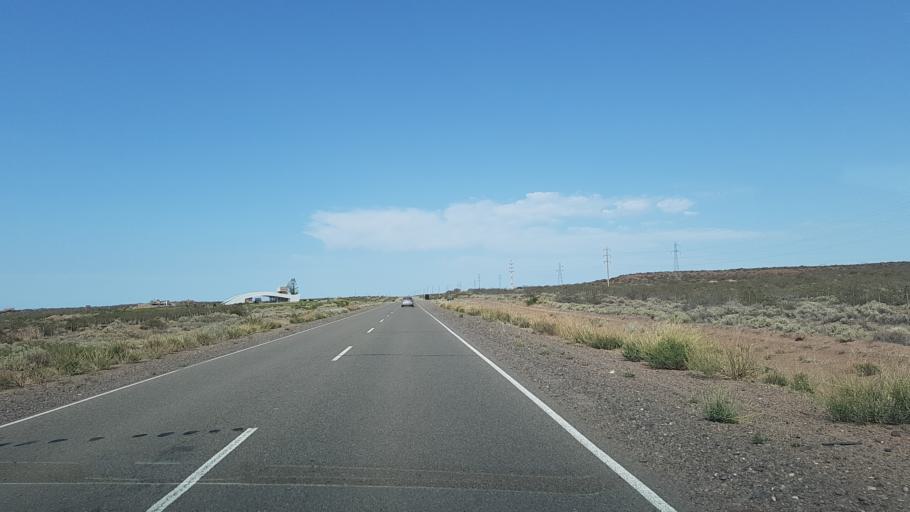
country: AR
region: Neuquen
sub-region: Departamento de Picun Leufu
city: Picun Leufu
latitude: -39.3304
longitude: -68.9699
